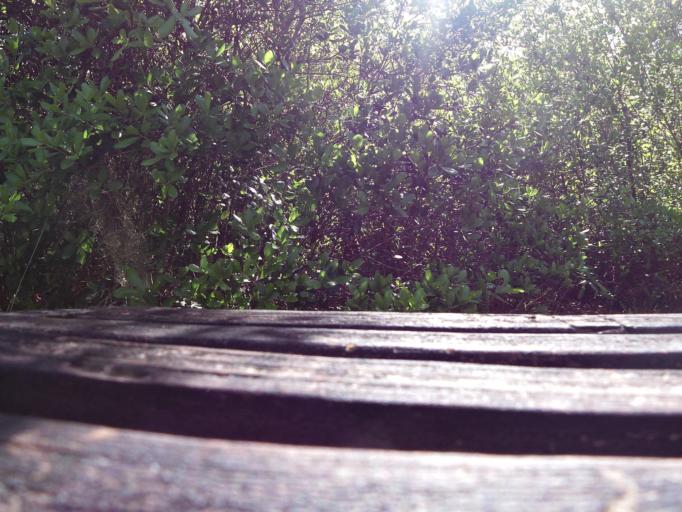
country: US
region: Florida
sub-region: Clay County
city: Keystone Heights
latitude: 29.8446
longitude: -81.9499
